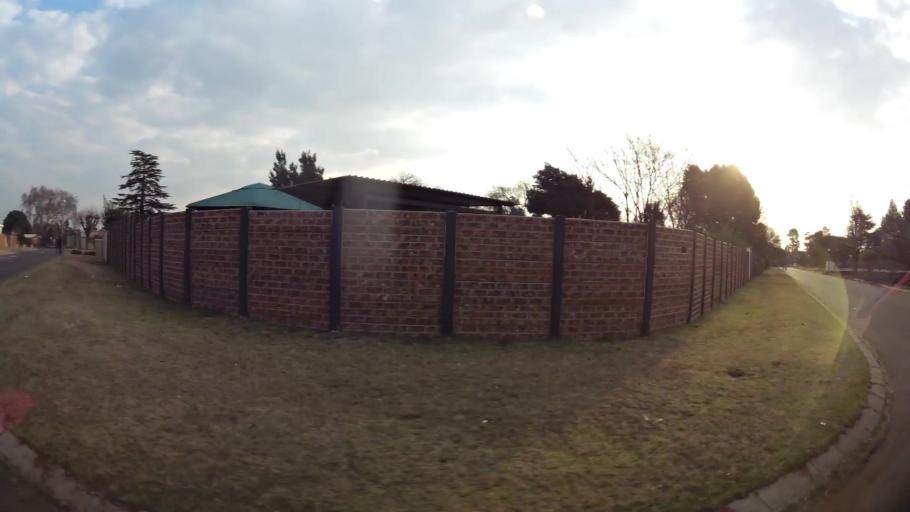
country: ZA
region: Gauteng
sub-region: Ekurhuleni Metropolitan Municipality
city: Benoni
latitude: -26.1578
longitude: 28.3006
